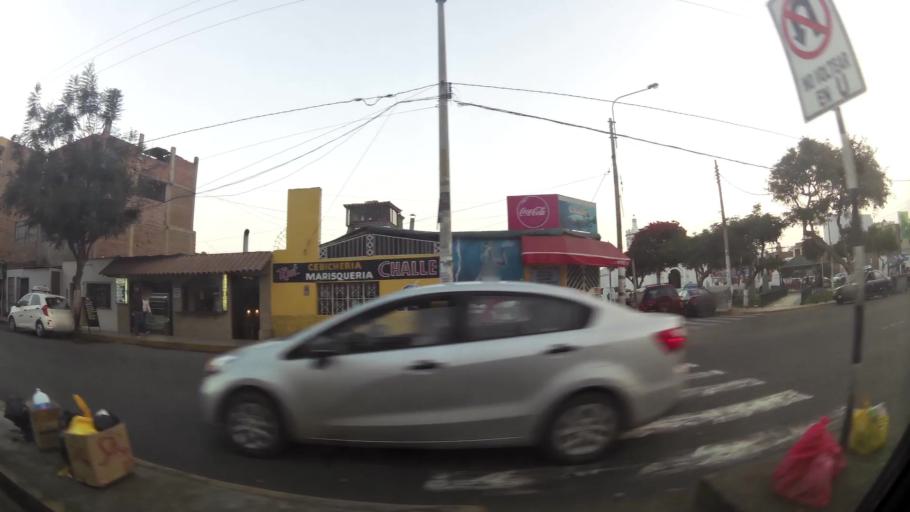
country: PE
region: La Libertad
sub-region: Provincia de Trujillo
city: Trujillo
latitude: -8.1019
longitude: -79.0429
